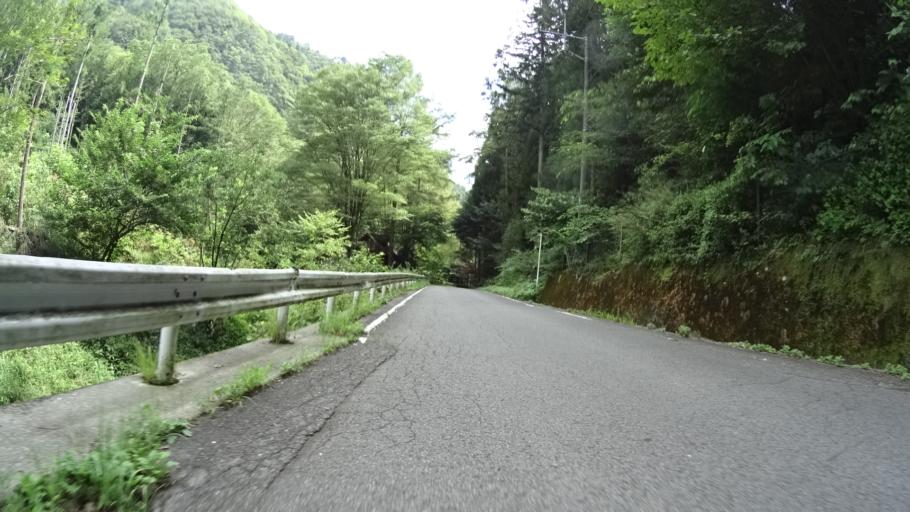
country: JP
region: Yamanashi
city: Nirasaki
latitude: 35.7769
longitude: 138.5348
